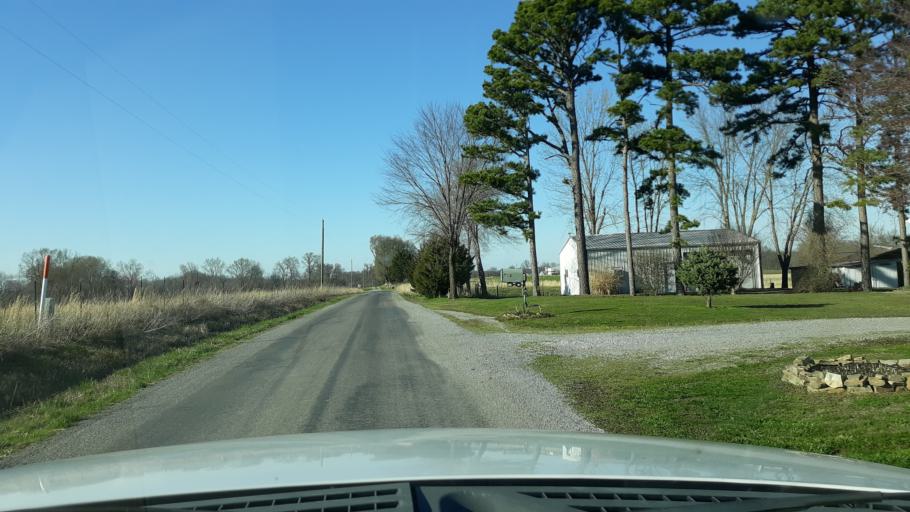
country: US
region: Illinois
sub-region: Saline County
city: Harrisburg
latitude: 37.7822
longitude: -88.6012
